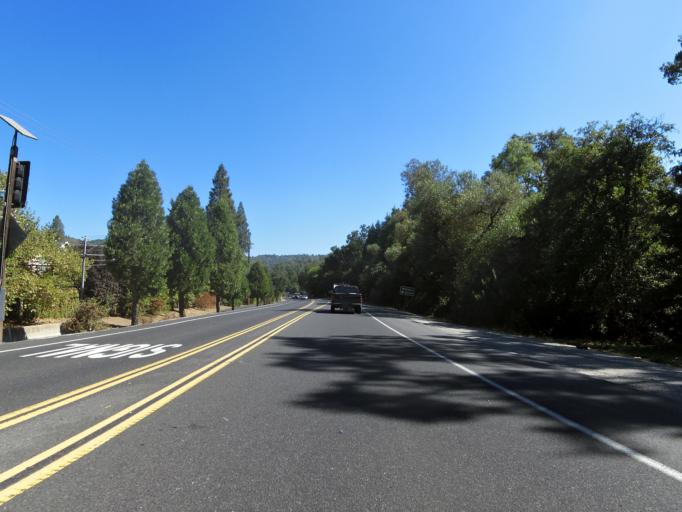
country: US
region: California
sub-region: Calaveras County
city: Murphys
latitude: 38.1401
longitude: -120.4548
